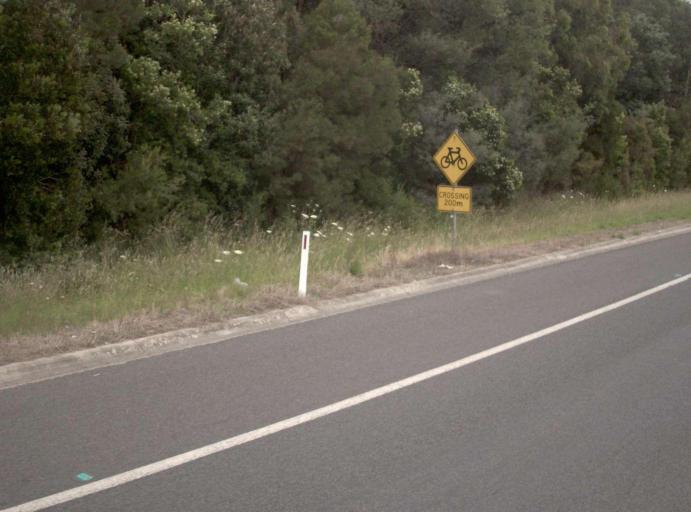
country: AU
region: Victoria
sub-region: Baw Baw
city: Warragul
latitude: -38.1753
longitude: 145.9753
